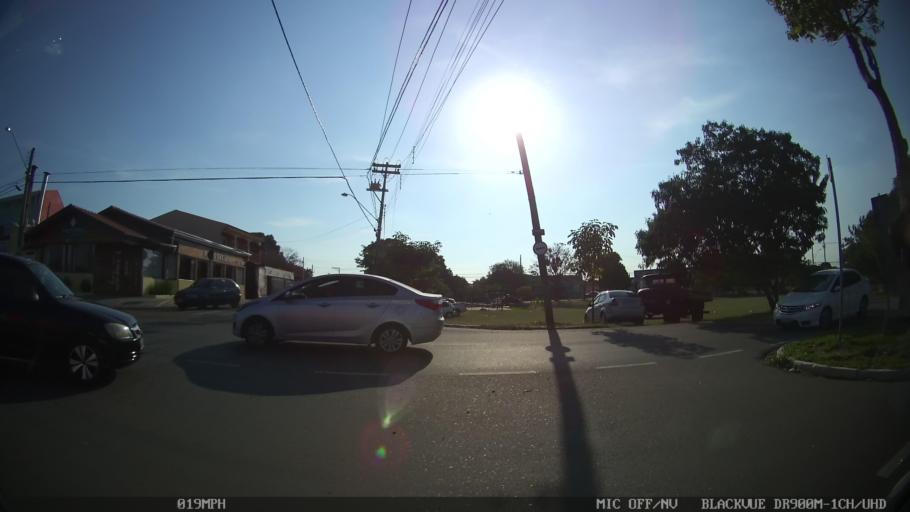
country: BR
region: Sao Paulo
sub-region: Campinas
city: Campinas
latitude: -22.9722
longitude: -47.1452
